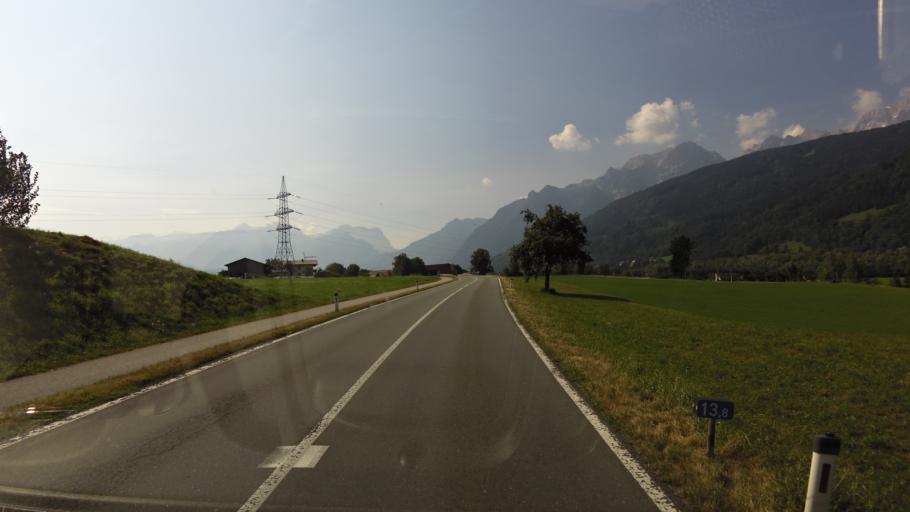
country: AT
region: Salzburg
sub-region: Politischer Bezirk Hallein
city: Kuchl
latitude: 47.6479
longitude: 13.1322
